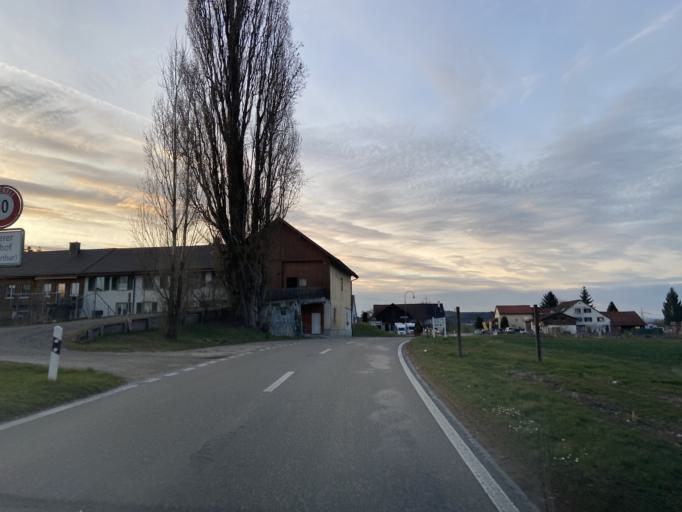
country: CH
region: Zurich
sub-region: Bezirk Winterthur
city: Wuelflingen (Kreis 6) / Lindenplatz
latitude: 47.5272
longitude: 8.6932
